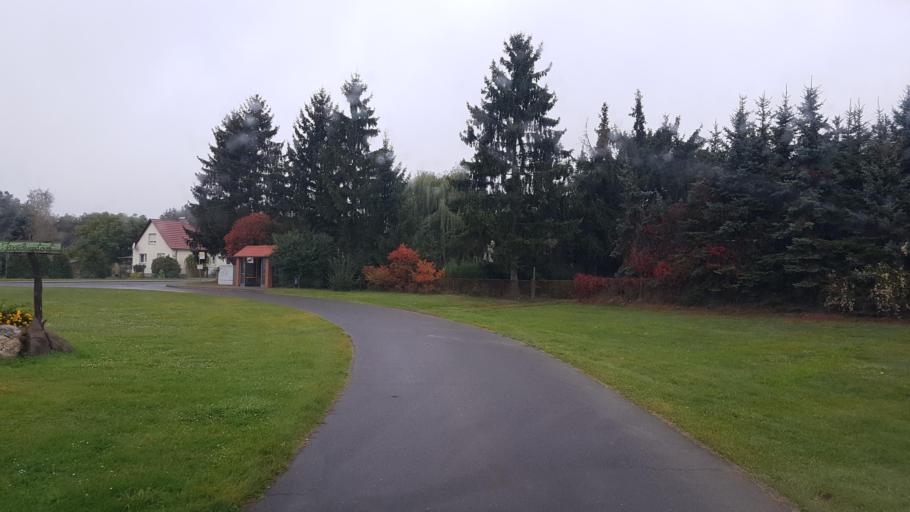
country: DE
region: Brandenburg
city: Furstenwalde
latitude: 52.4314
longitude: 14.0187
